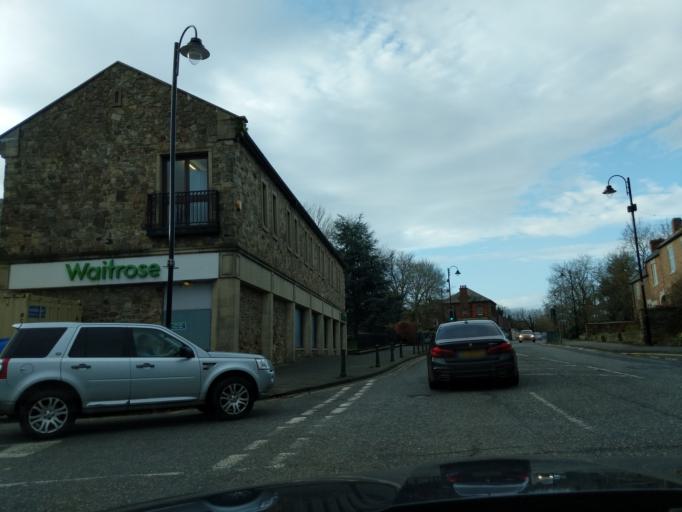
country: GB
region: England
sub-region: Northumberland
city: Ponteland
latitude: 55.0496
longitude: -1.7436
